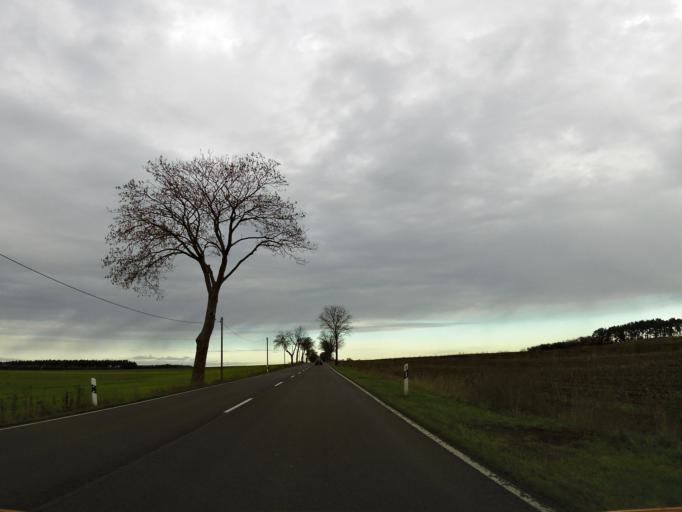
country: DE
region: Saxony-Anhalt
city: Letzlingen
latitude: 52.4285
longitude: 11.4833
